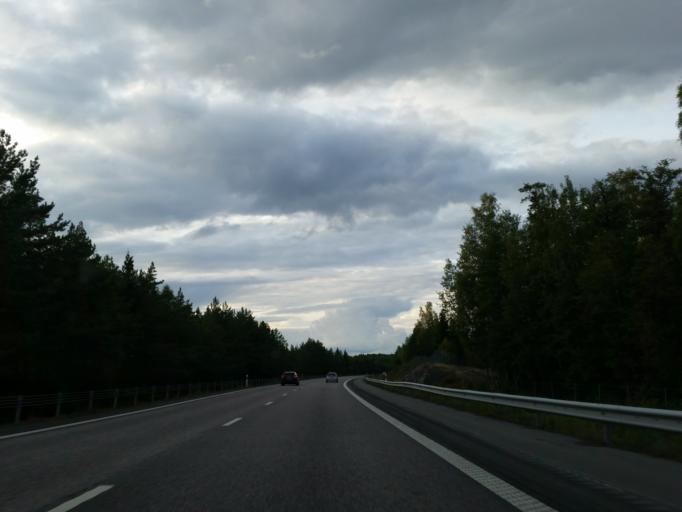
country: SE
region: Uppsala
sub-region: Knivsta Kommun
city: Knivsta
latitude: 59.7029
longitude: 17.8568
